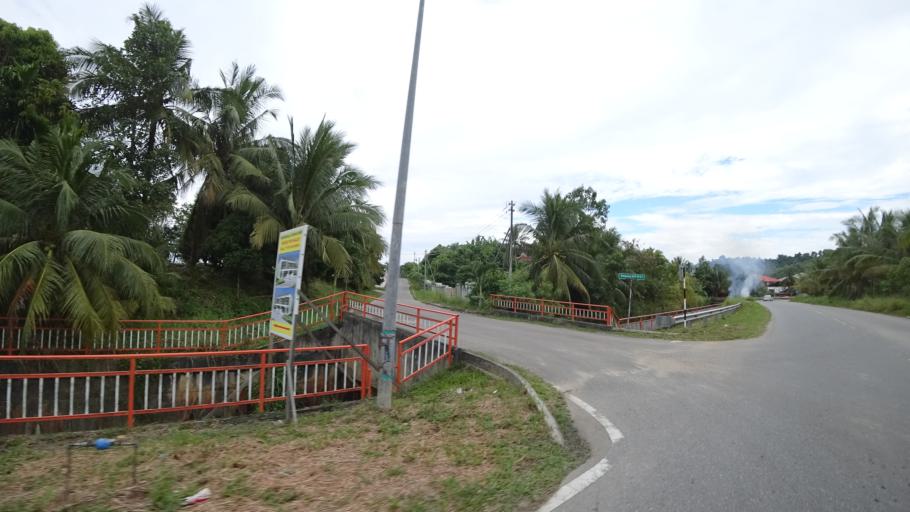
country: BN
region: Brunei and Muara
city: Bandar Seri Begawan
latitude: 4.8771
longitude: 114.8673
